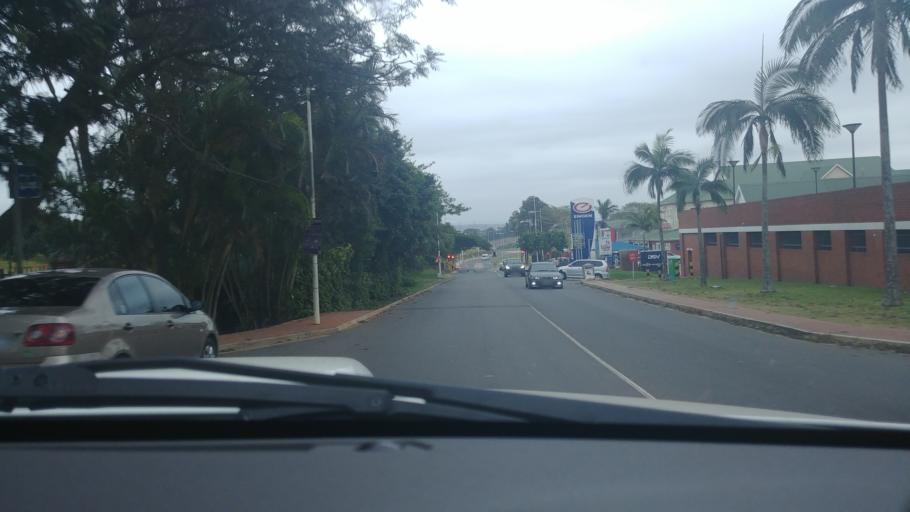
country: ZA
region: KwaZulu-Natal
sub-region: eThekwini Metropolitan Municipality
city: Durban
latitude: -29.7155
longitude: 31.0526
